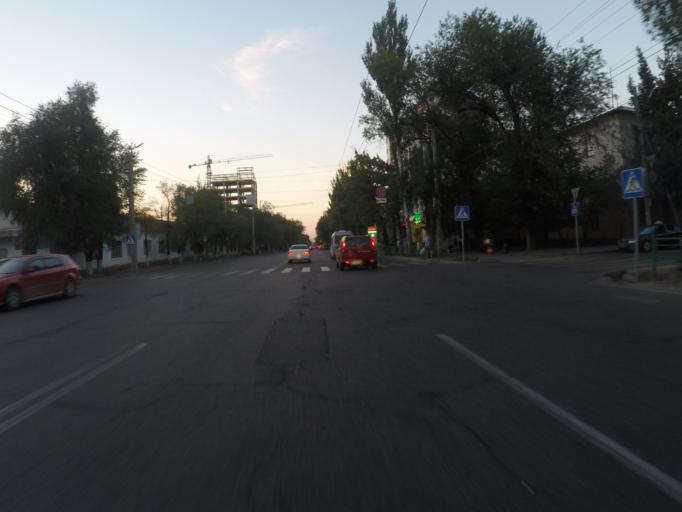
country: KG
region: Chuy
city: Bishkek
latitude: 42.8497
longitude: 74.6096
